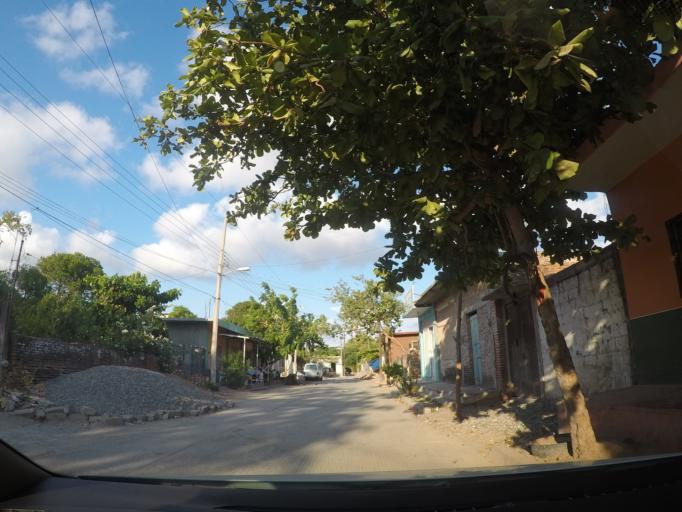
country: MX
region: Oaxaca
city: Juchitan de Zaragoza
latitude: 16.4359
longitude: -95.0271
